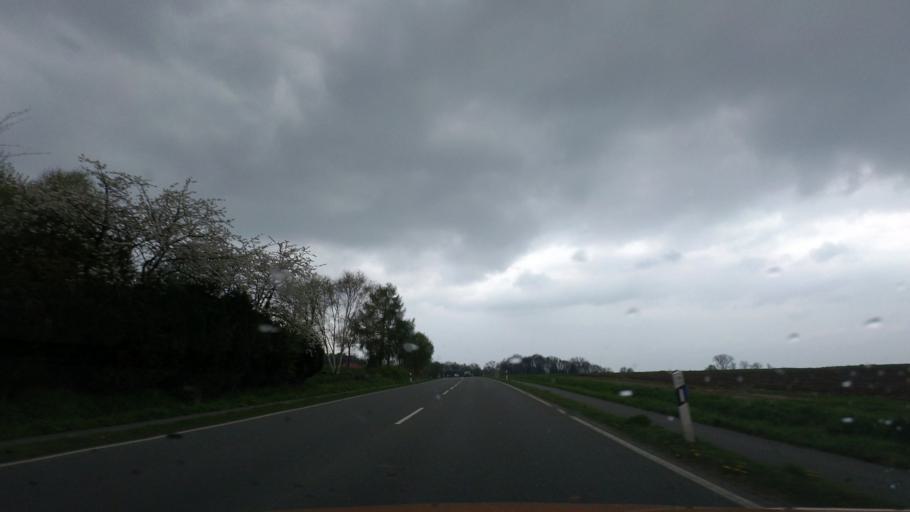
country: DE
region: Lower Saxony
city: Alfhausen
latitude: 52.5162
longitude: 7.9462
